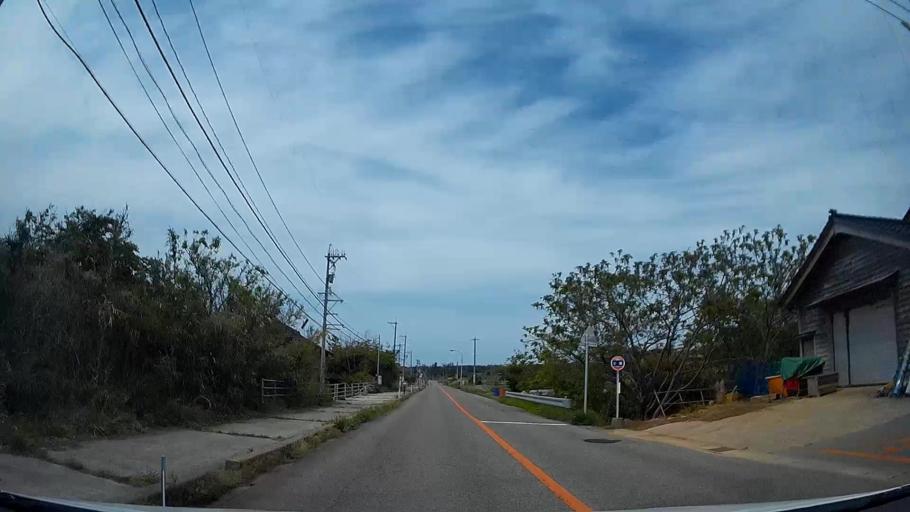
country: JP
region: Ishikawa
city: Hakui
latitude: 37.0291
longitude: 136.7474
